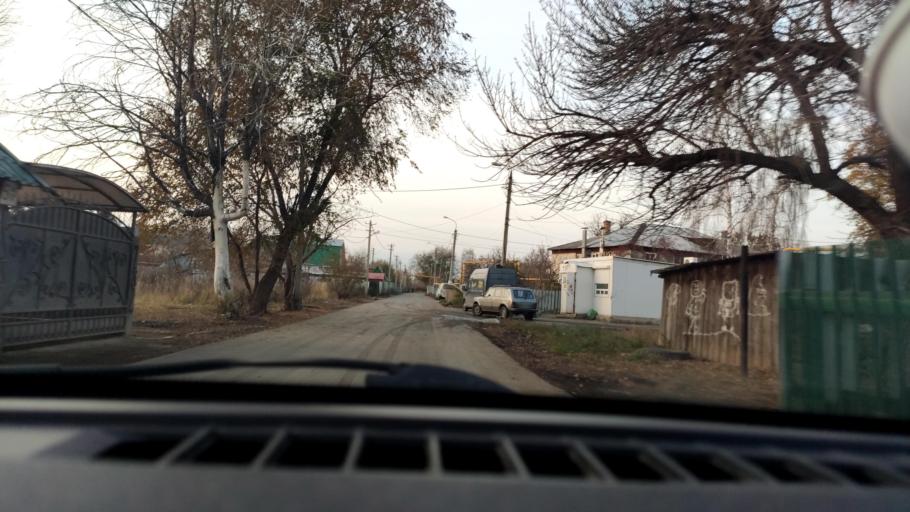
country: RU
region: Samara
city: Samara
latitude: 53.1399
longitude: 50.1349
